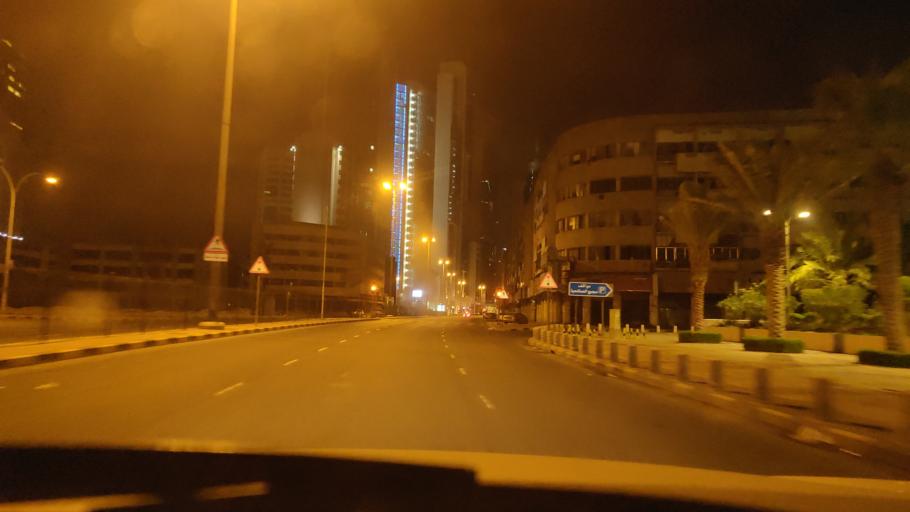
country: KW
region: Al Asimah
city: Kuwait City
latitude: 29.3634
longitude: 47.9651
